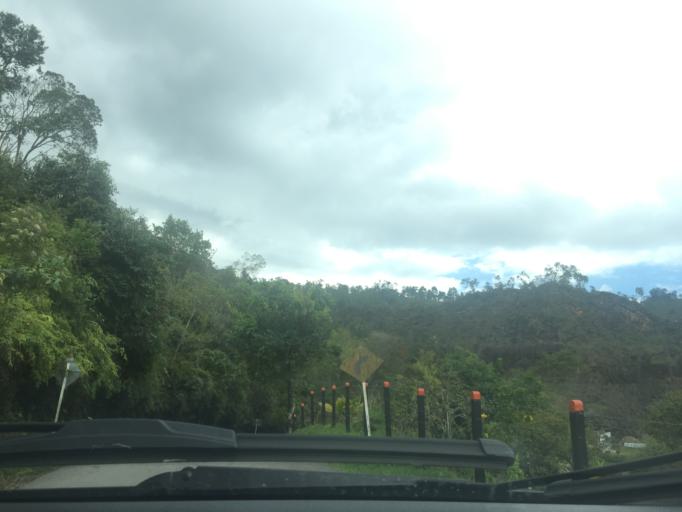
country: CO
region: Cundinamarca
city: Supata
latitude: 5.0541
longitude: -74.2356
